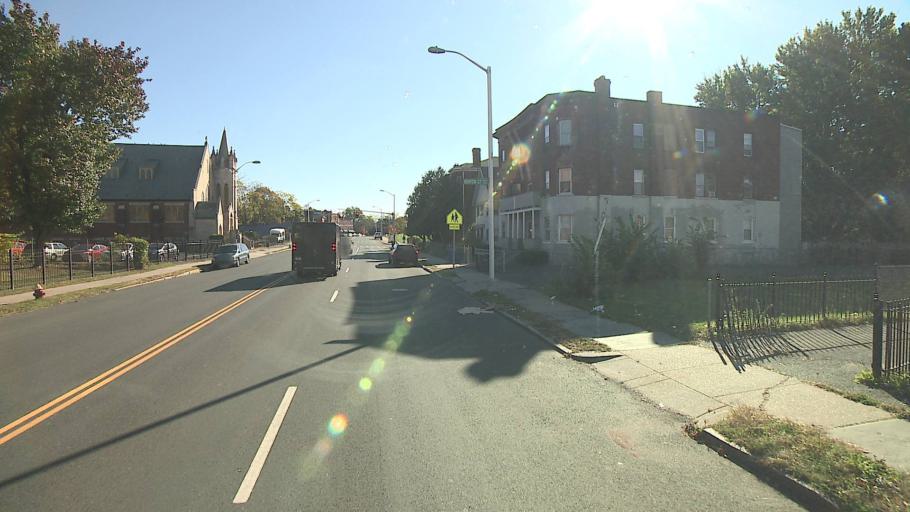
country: US
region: Connecticut
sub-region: Hartford County
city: Hartford
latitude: 41.7771
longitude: -72.6832
